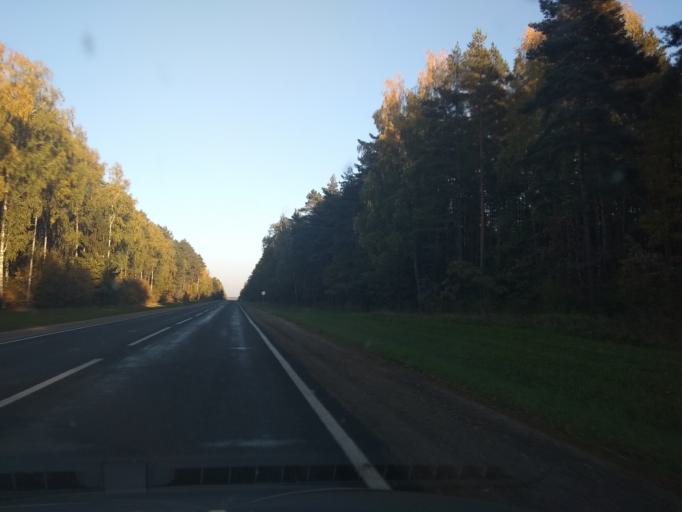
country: BY
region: Grodnenskaya
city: Vawkavysk
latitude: 53.1471
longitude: 24.5241
